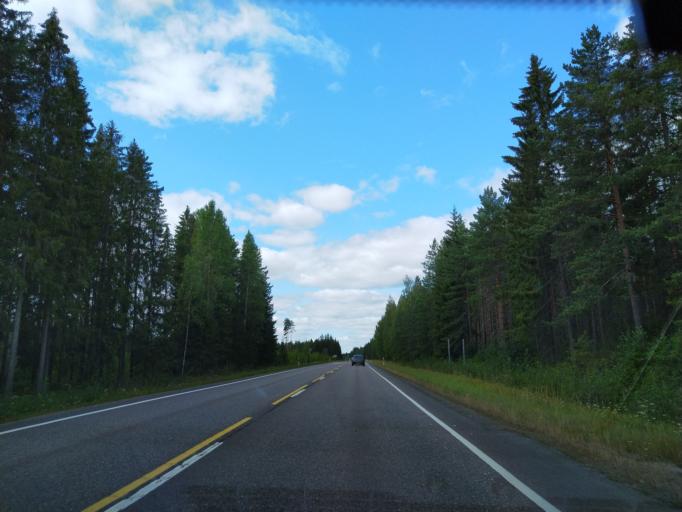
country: FI
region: Haeme
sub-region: Haemeenlinna
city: Renko
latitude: 60.7621
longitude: 24.2795
